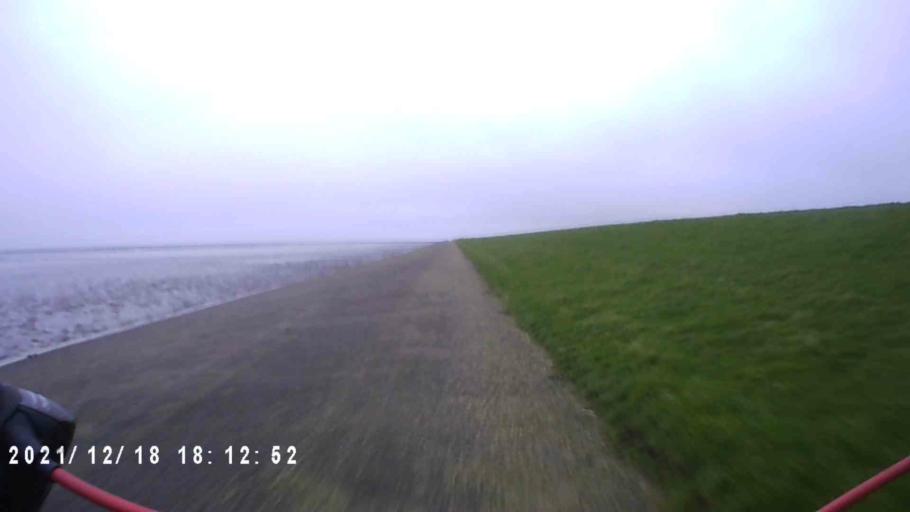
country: NL
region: Friesland
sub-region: Gemeente Dongeradeel
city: Ternaard
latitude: 53.3916
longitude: 5.9515
